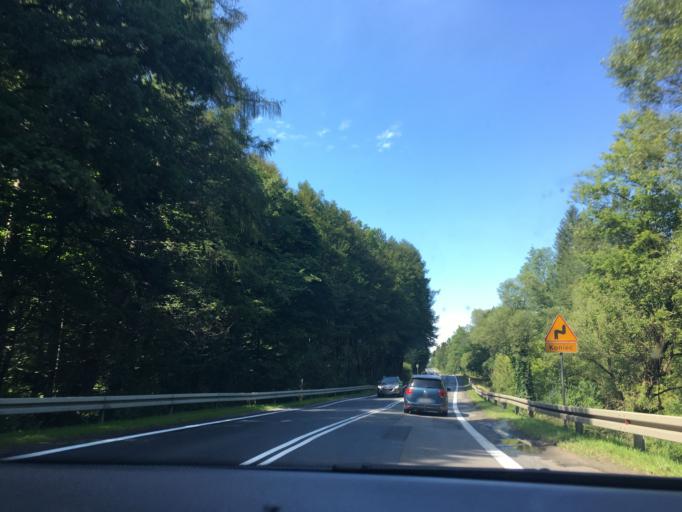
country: PL
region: Subcarpathian Voivodeship
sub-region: Powiat krosnienski
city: Dukla
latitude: 49.4786
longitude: 21.7080
